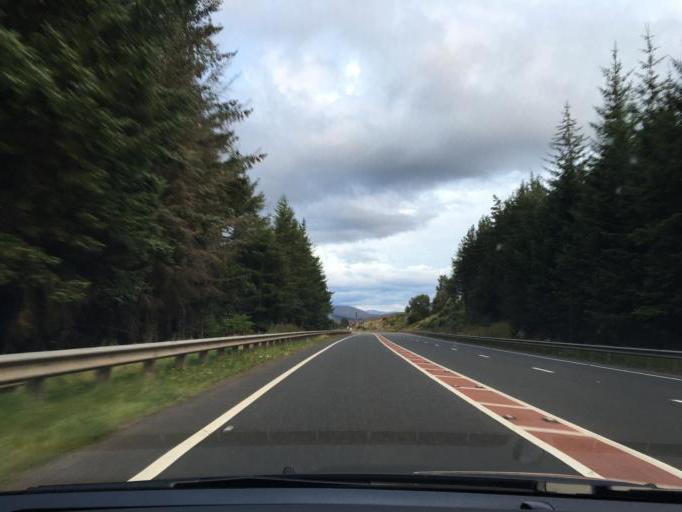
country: GB
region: Scotland
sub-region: Highland
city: Inverness
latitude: 57.3759
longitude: -4.0374
